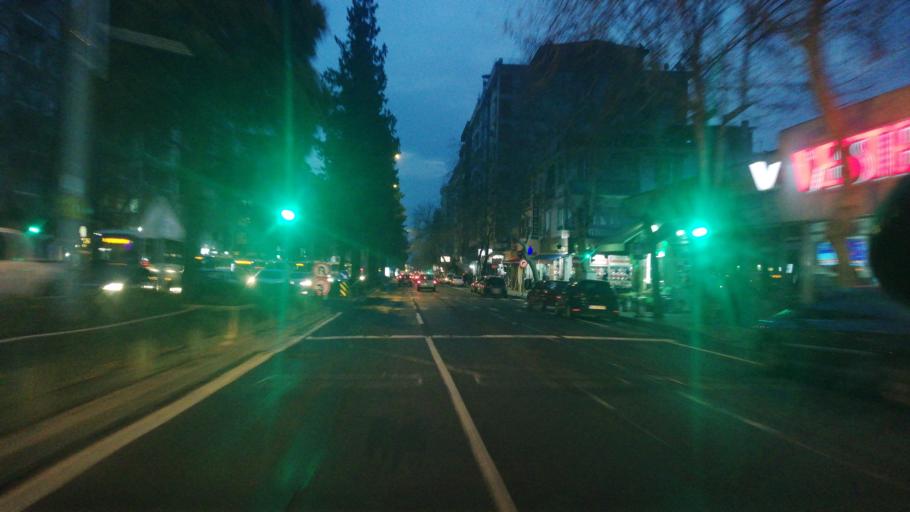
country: TR
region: Kahramanmaras
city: Kahramanmaras
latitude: 37.5803
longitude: 36.9272
